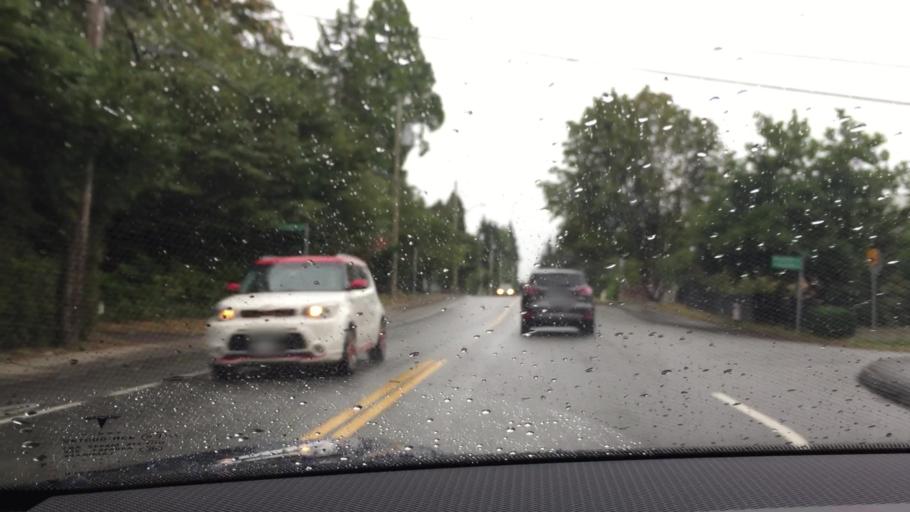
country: CA
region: British Columbia
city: Burnaby
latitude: 49.2327
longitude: -122.9595
